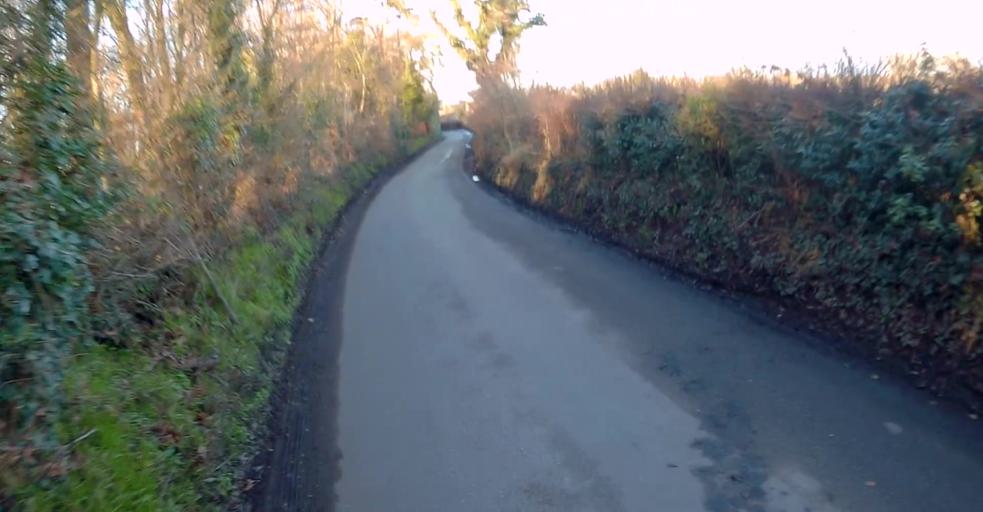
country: GB
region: England
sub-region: Hampshire
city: Hook
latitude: 51.2972
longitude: -0.9822
